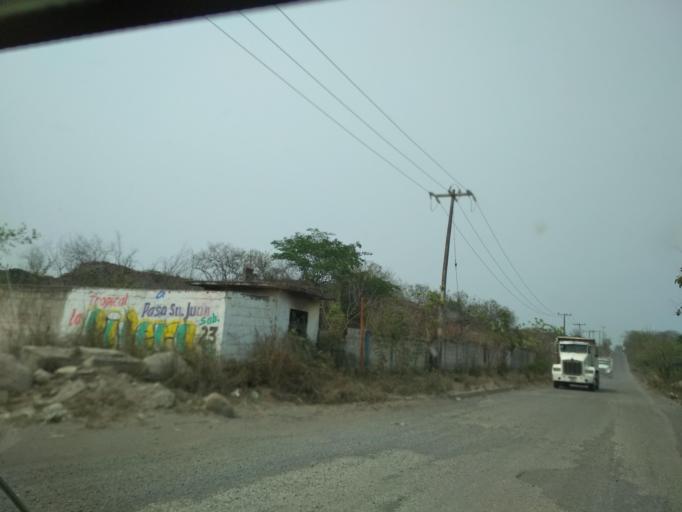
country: MX
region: Veracruz
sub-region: Veracruz
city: Delfino Victoria (Santa Fe)
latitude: 19.1848
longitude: -96.3183
